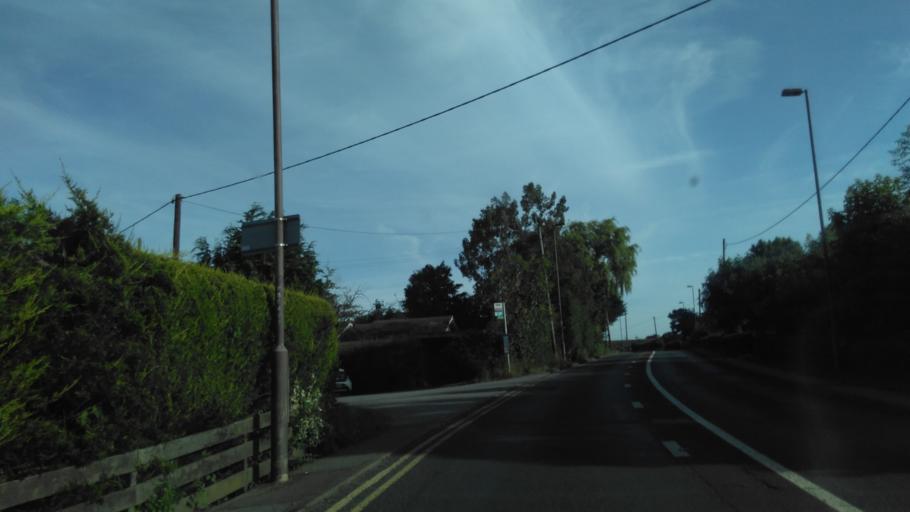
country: GB
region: England
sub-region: Kent
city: Blean
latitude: 51.3039
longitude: 1.0449
